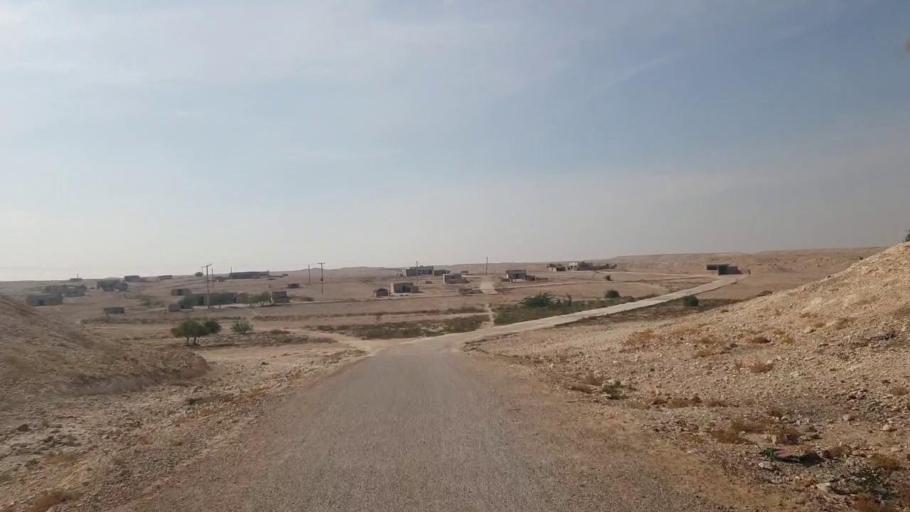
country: PK
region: Sindh
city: Hala
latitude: 25.7800
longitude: 68.2786
